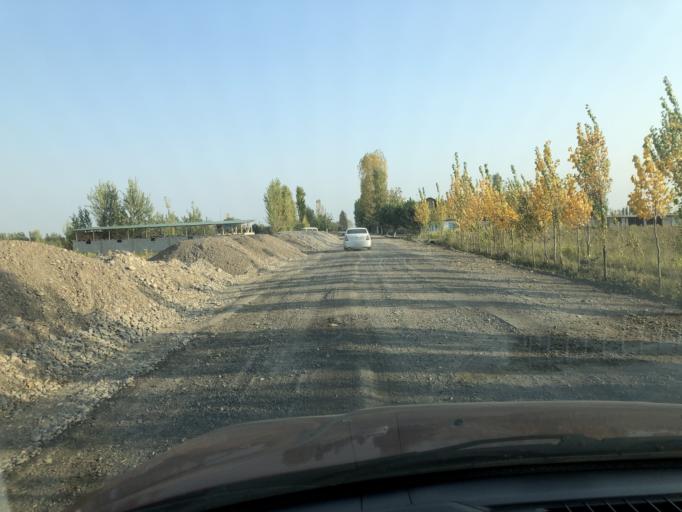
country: UZ
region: Namangan
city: Uychi
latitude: 41.0665
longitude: 71.9854
